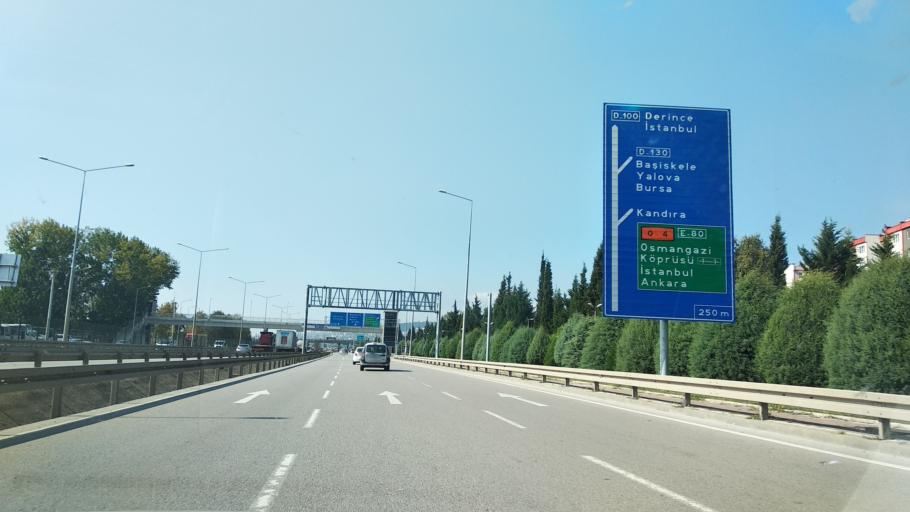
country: TR
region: Kocaeli
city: Kullar
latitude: 40.7610
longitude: 29.9726
